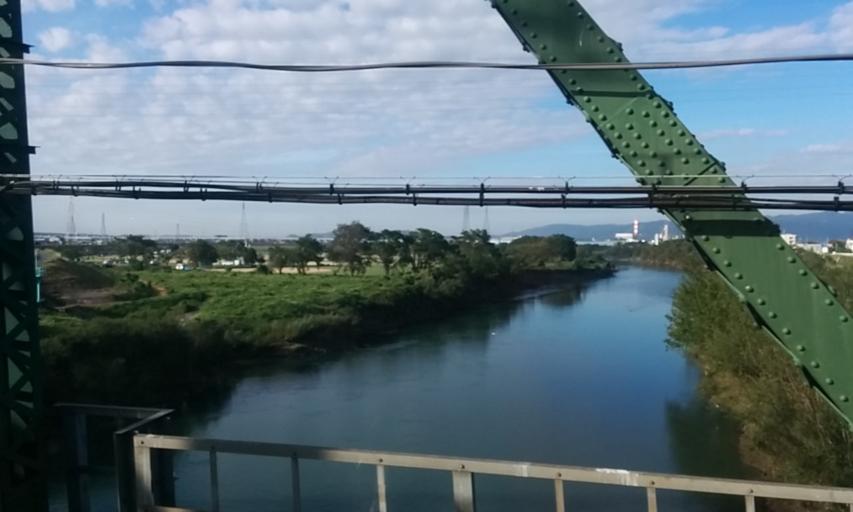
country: JP
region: Kyoto
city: Uji
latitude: 34.9257
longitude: 135.7655
